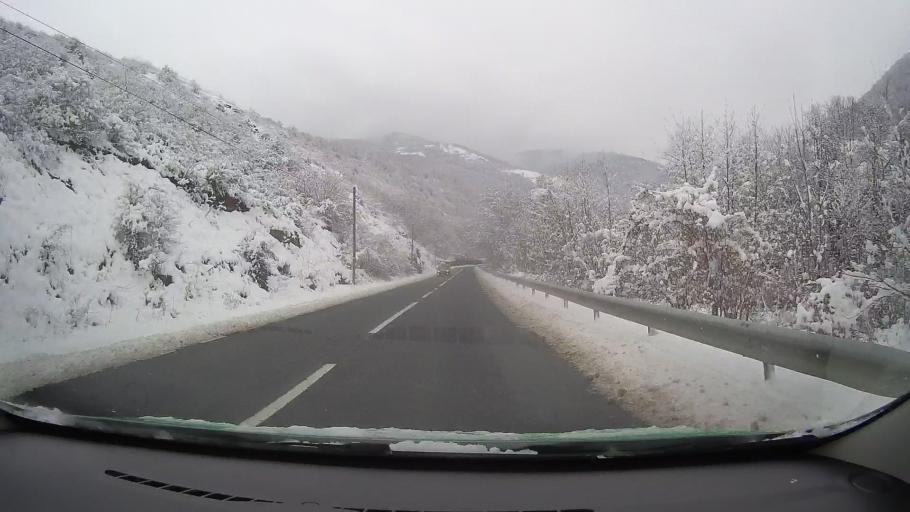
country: RO
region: Alba
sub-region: Comuna Sasciori
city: Sasciori
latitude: 45.8298
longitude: 23.6022
